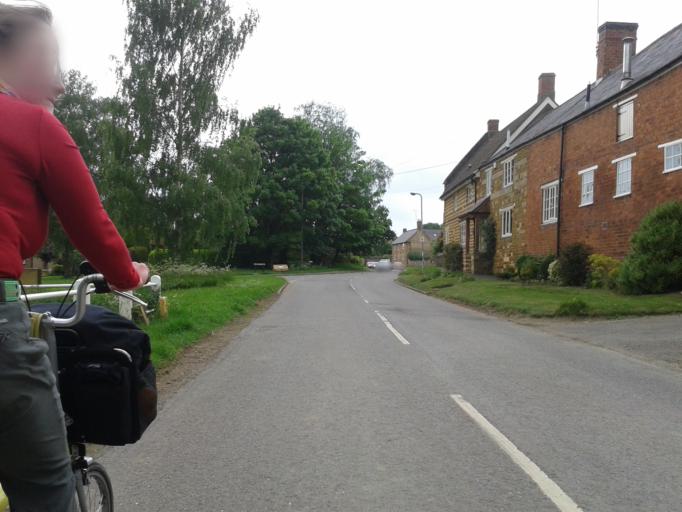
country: GB
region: England
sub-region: Northamptonshire
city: Desborough
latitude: 52.5105
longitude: -0.8238
